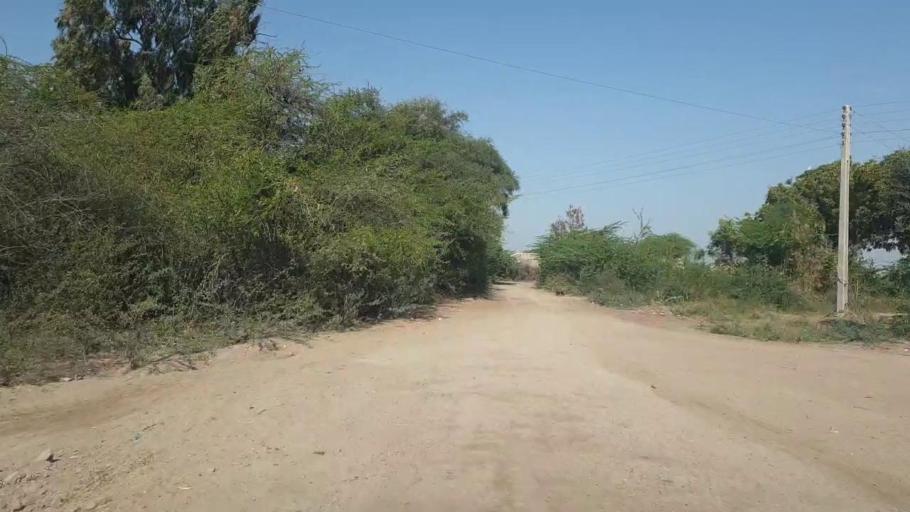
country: PK
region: Sindh
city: Umarkot
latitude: 25.2912
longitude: 69.6492
